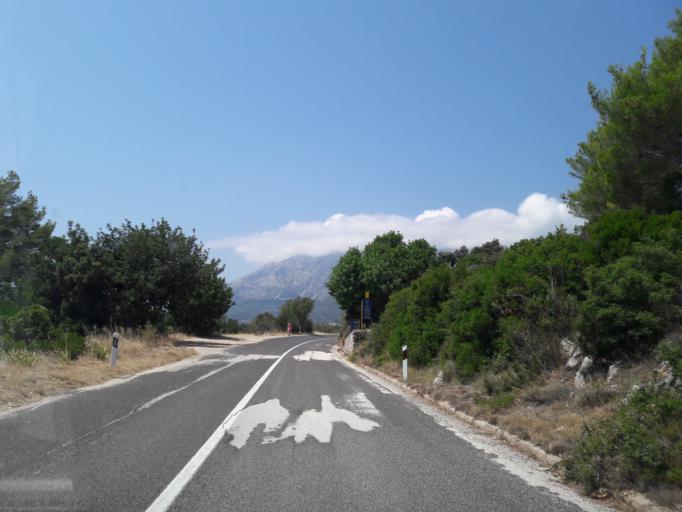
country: HR
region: Dubrovacko-Neretvanska
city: Orebic
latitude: 42.9769
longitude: 17.2295
